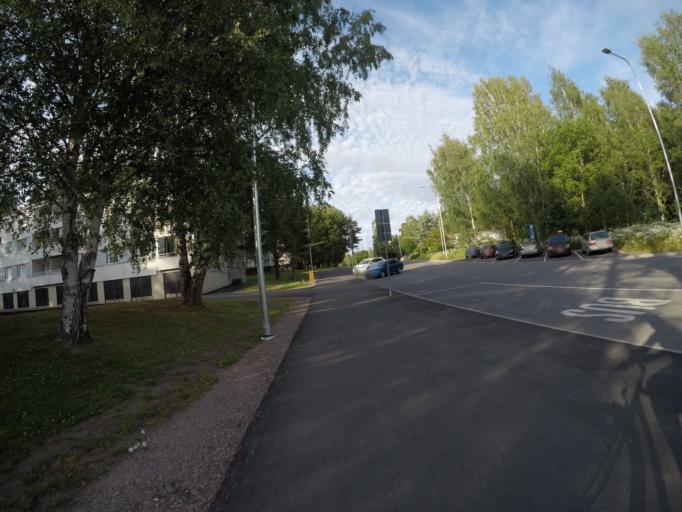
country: FI
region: Haeme
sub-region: Haemeenlinna
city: Haemeenlinna
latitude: 60.9821
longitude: 24.4057
